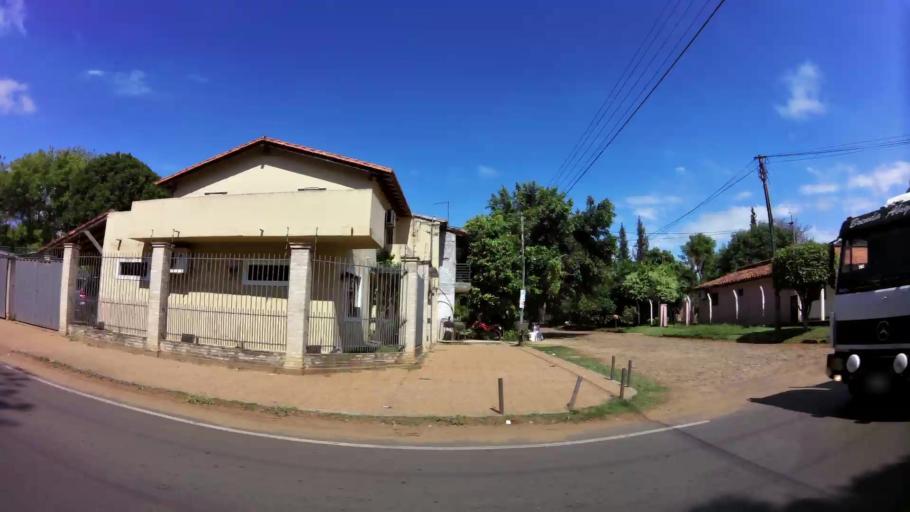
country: PY
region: Central
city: San Lorenzo
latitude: -25.2557
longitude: -57.4997
